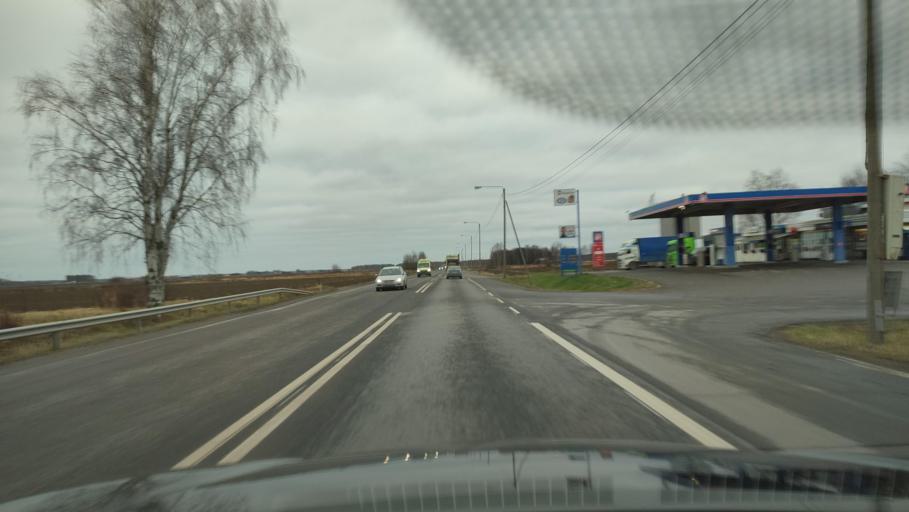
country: FI
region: Southern Ostrobothnia
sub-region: Seinaejoki
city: Ilmajoki
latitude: 62.7331
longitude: 22.6039
